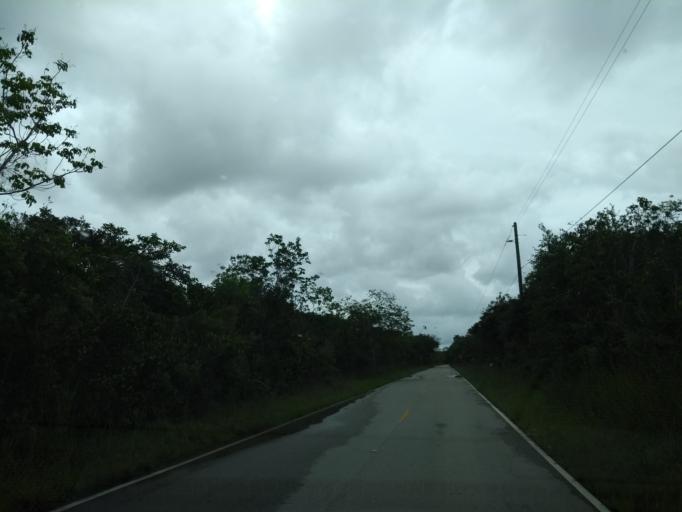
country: US
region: Florida
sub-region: Miami-Dade County
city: The Hammocks
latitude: 25.7612
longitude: -80.9172
